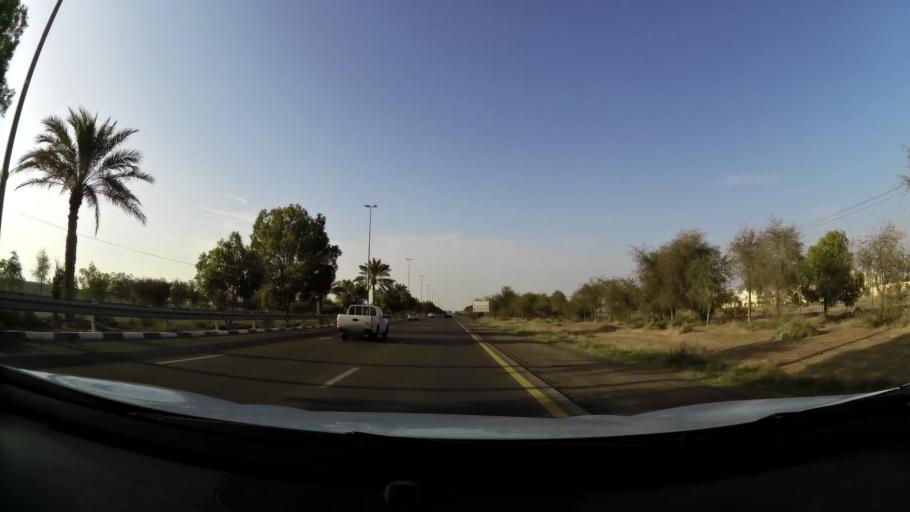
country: AE
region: Abu Dhabi
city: Al Ain
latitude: 24.1025
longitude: 55.8277
